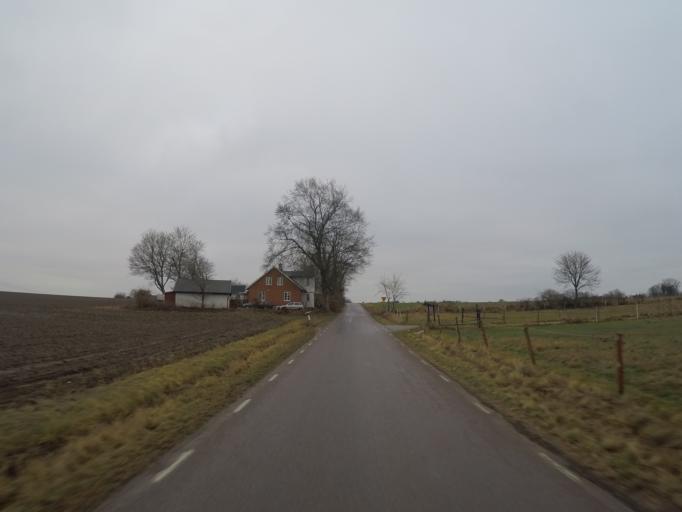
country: SE
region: Skane
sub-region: Hoors Kommun
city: Loberod
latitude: 55.7464
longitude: 13.4131
